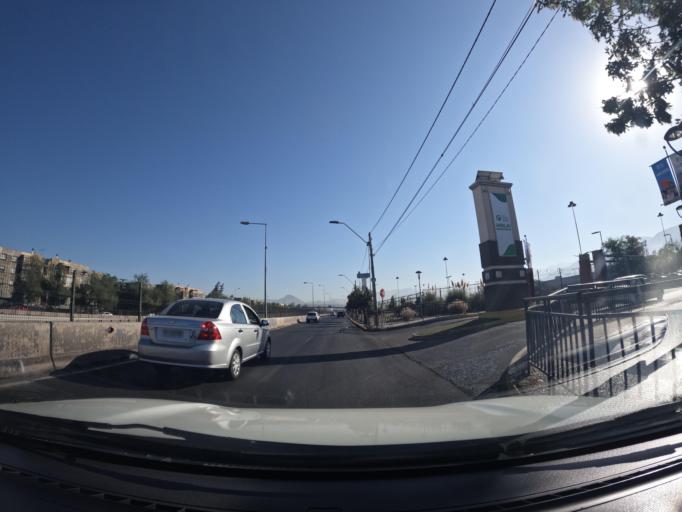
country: CL
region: Santiago Metropolitan
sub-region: Provincia de Santiago
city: Villa Presidente Frei, Nunoa, Santiago, Chile
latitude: -33.4855
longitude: -70.5787
